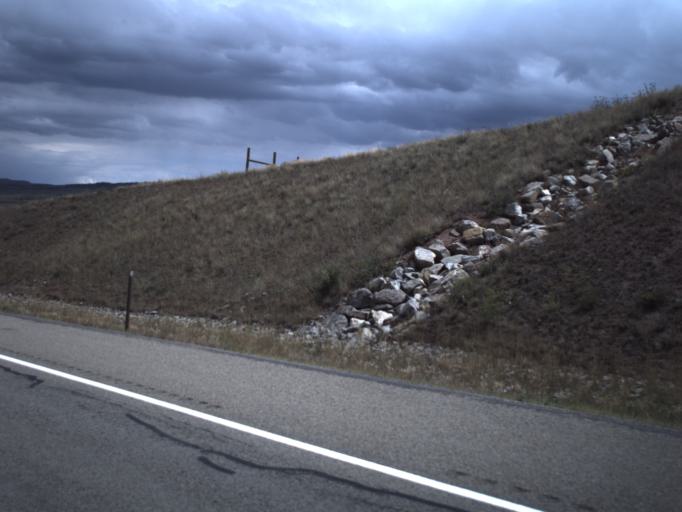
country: US
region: Utah
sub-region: Carbon County
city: Helper
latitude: 39.8448
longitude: -111.0007
